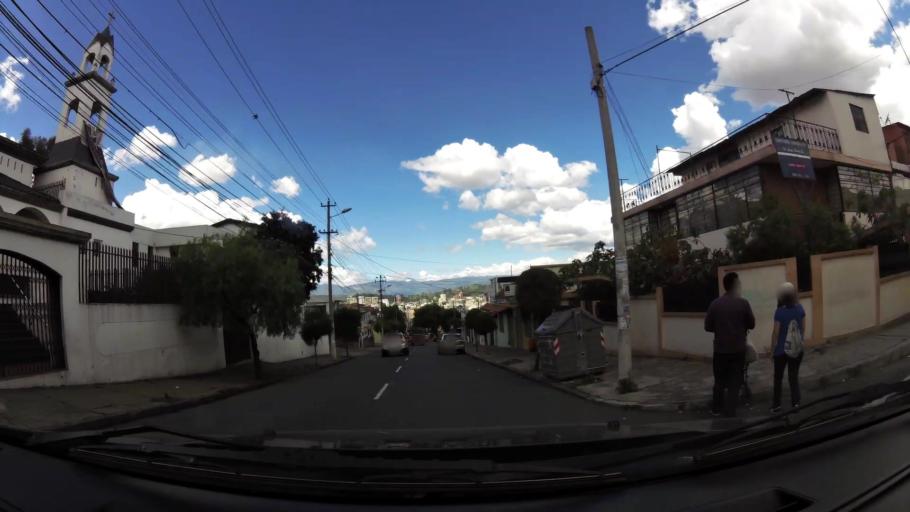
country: EC
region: Pichincha
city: Quito
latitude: -0.1900
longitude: -78.5008
